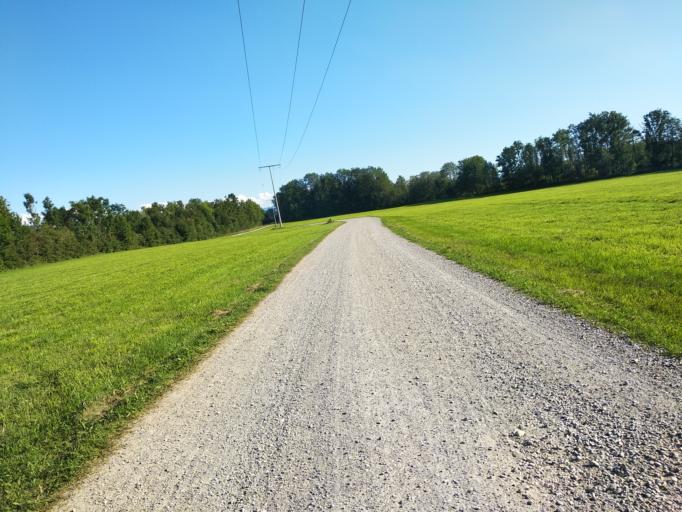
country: DE
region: Baden-Wuerttemberg
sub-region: Tuebingen Region
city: Leutkirch im Allgau
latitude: 47.7708
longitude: 10.0440
